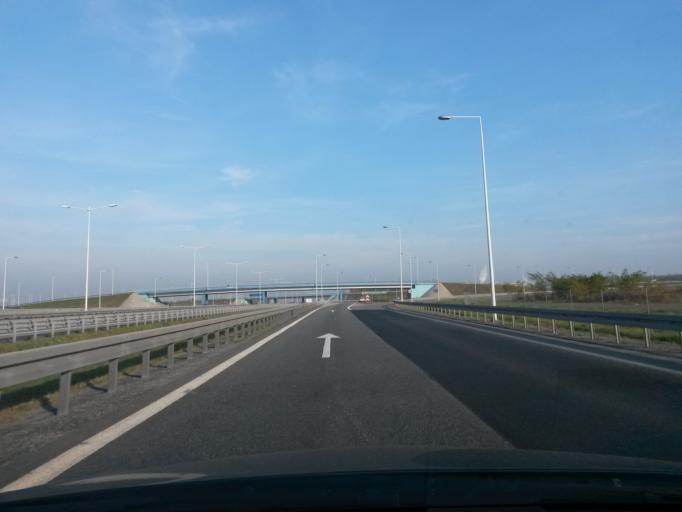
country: PL
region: Lower Silesian Voivodeship
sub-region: Powiat wroclawski
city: Tyniec Maly
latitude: 51.0432
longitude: 16.9287
